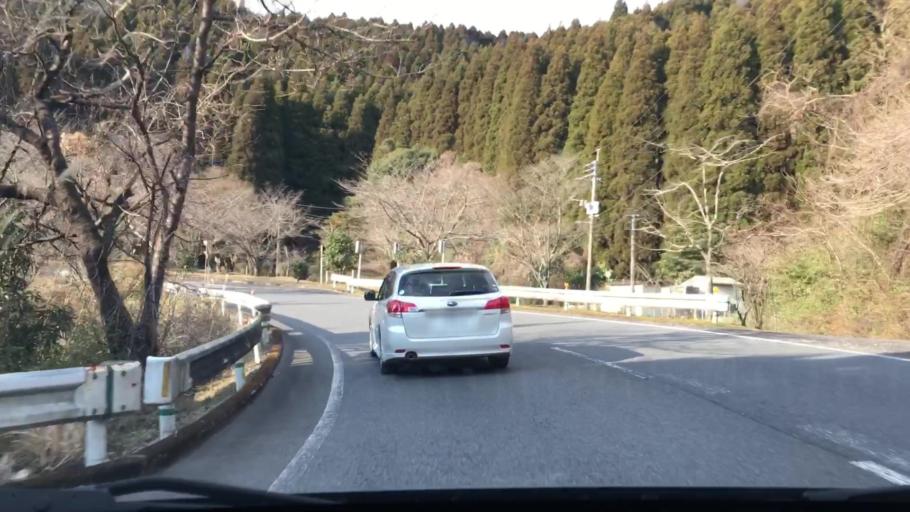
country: JP
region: Miyazaki
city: Miyazaki-shi
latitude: 31.7763
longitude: 131.3330
